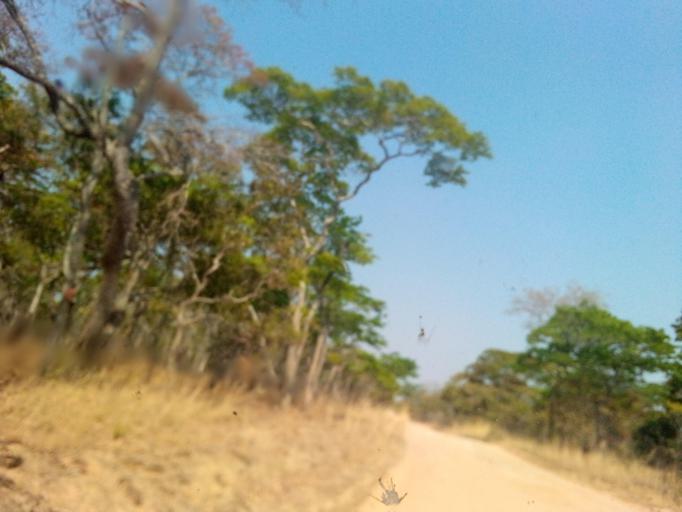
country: ZM
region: Northern
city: Mpika
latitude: -12.2419
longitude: 30.8600
